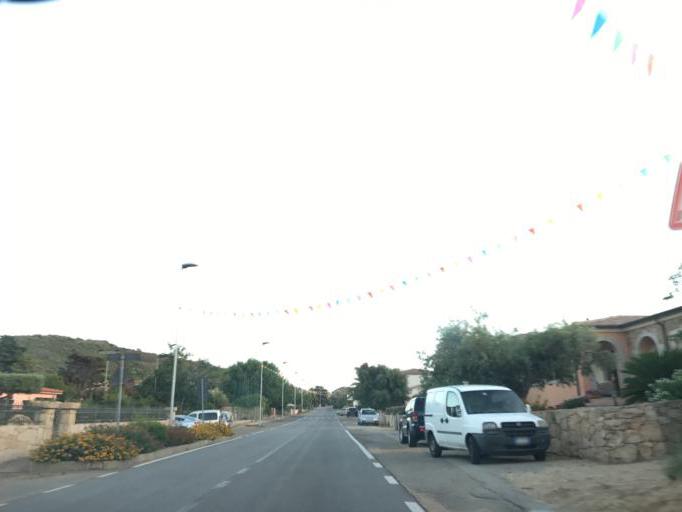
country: IT
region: Sardinia
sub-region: Provincia di Olbia-Tempio
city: San Teodoro
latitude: 40.7482
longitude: 9.6470
